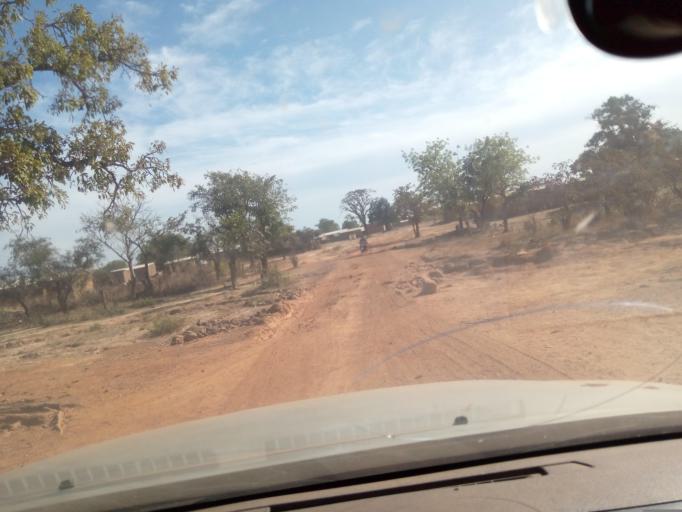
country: ML
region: Sikasso
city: Sikasso
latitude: 11.4648
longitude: -5.3239
